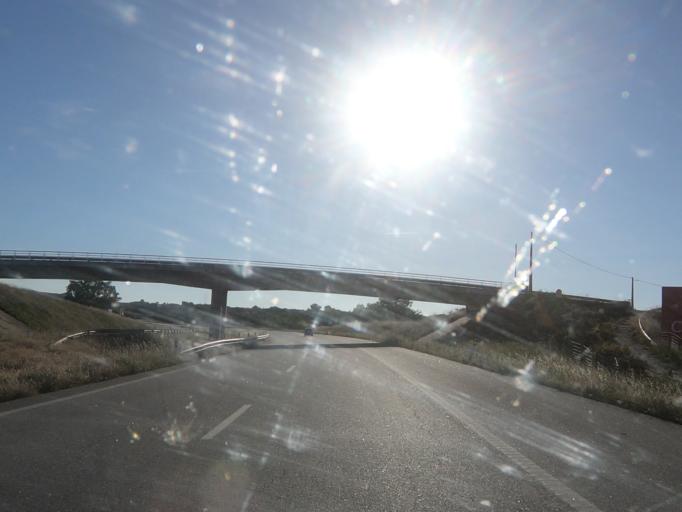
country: PT
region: Guarda
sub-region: Guarda
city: Sequeira
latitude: 40.6027
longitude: -7.1015
